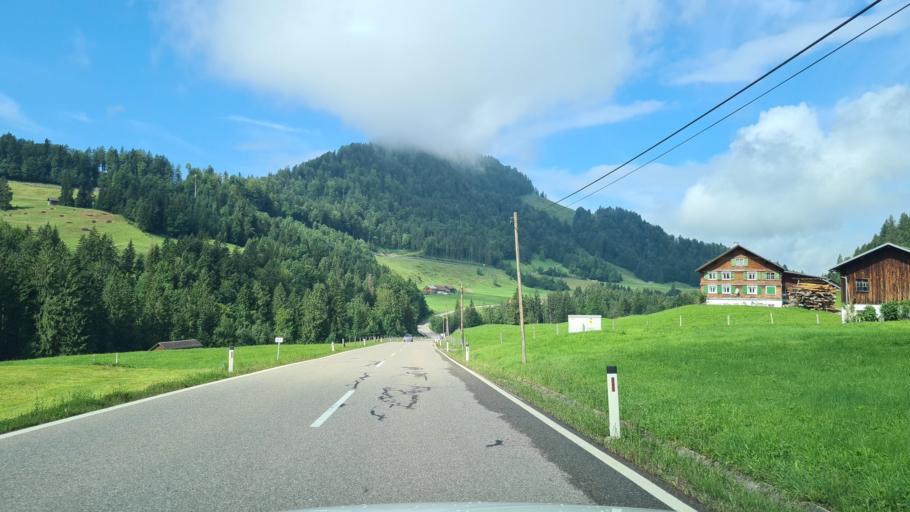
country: AT
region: Vorarlberg
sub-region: Politischer Bezirk Bregenz
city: Sibratsgfall
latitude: 47.4481
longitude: 10.0166
